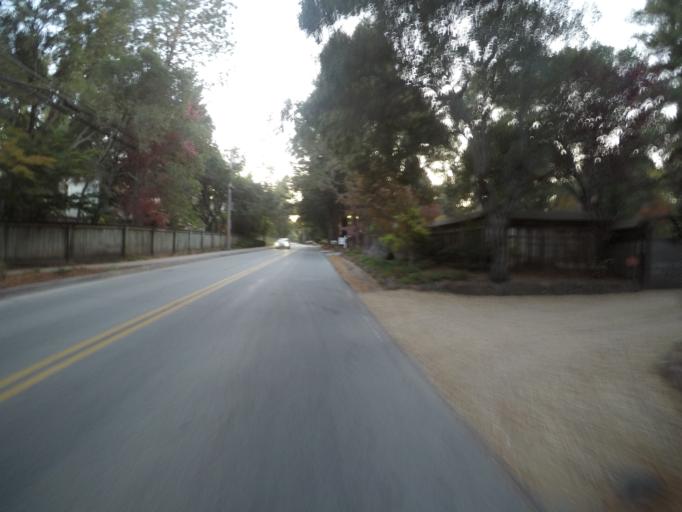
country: US
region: California
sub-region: Santa Cruz County
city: Mount Hermon
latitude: 37.0400
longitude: -122.0398
